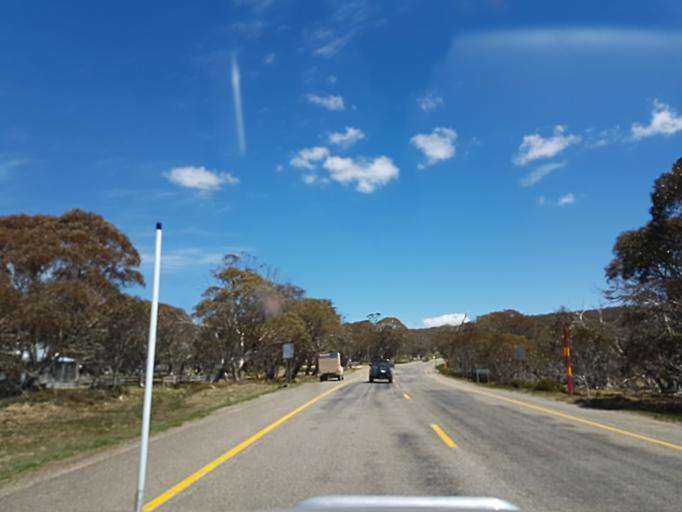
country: AU
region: Victoria
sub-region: Alpine
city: Mount Beauty
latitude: -37.0209
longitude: 147.2407
